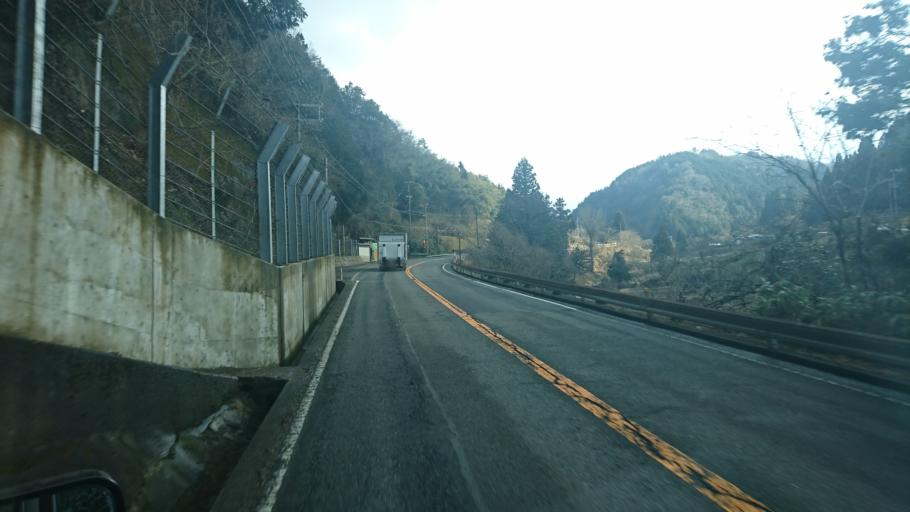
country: JP
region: Tottori
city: Tottori
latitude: 35.5394
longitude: 134.5096
